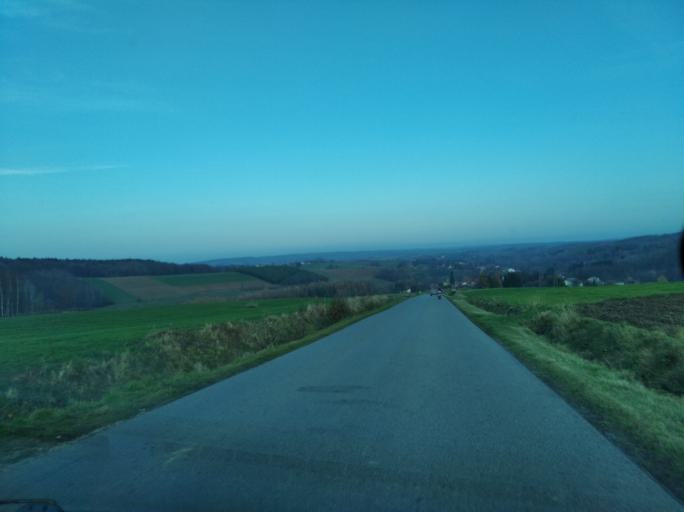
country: PL
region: Subcarpathian Voivodeship
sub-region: Powiat ropczycko-sedziszowski
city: Iwierzyce
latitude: 49.9877
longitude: 21.7212
